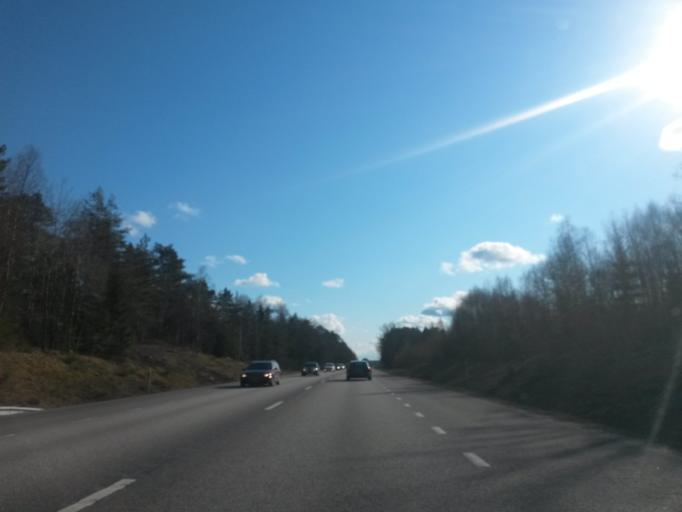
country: SE
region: Vaestra Goetaland
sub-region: Vargarda Kommun
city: Vargarda
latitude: 58.1240
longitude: 12.8524
